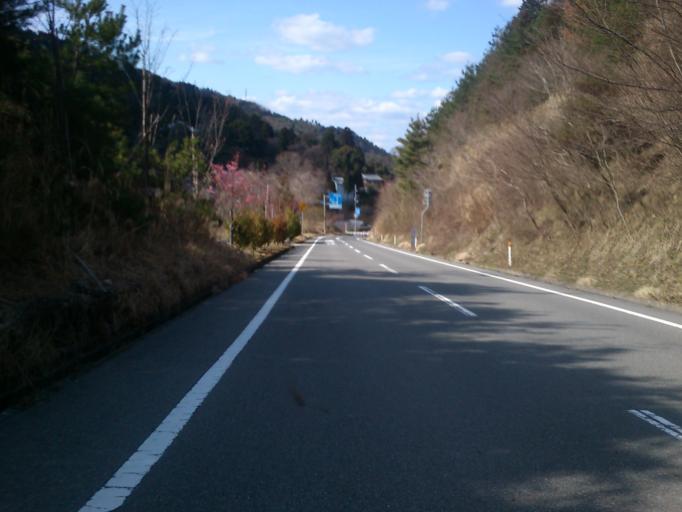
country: JP
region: Kyoto
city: Yawata
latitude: 34.9116
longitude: 135.6536
